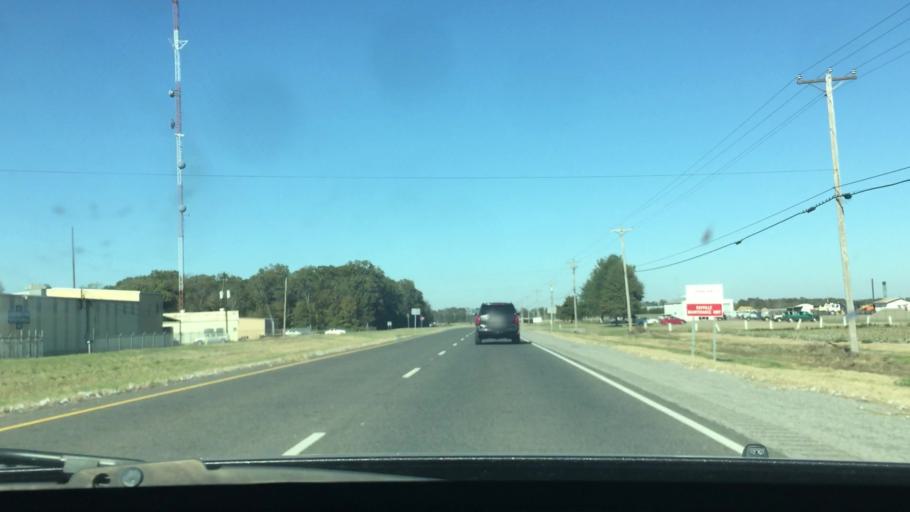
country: US
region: Louisiana
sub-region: Richland Parish
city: Rayville
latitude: 32.4182
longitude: -91.7640
